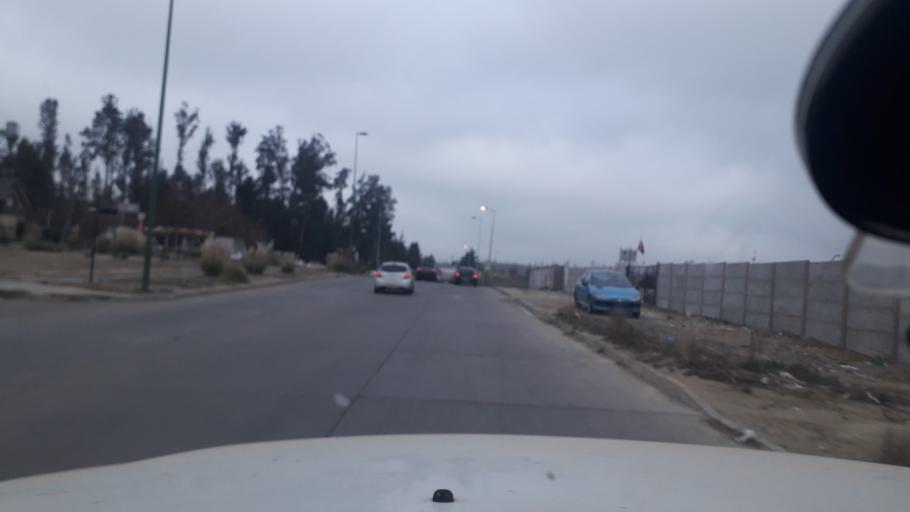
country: CL
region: Valparaiso
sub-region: Provincia de Valparaiso
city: Vina del Mar
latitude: -33.1296
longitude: -71.5653
